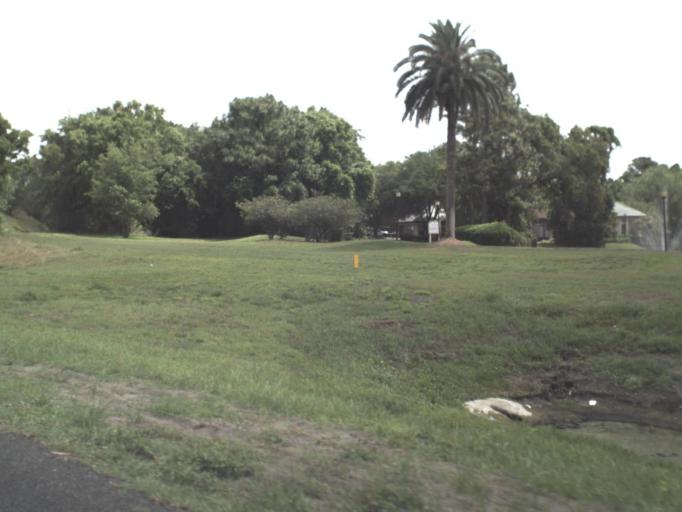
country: US
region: Florida
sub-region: Saint Johns County
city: Fruit Cove
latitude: 30.2014
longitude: -81.5517
